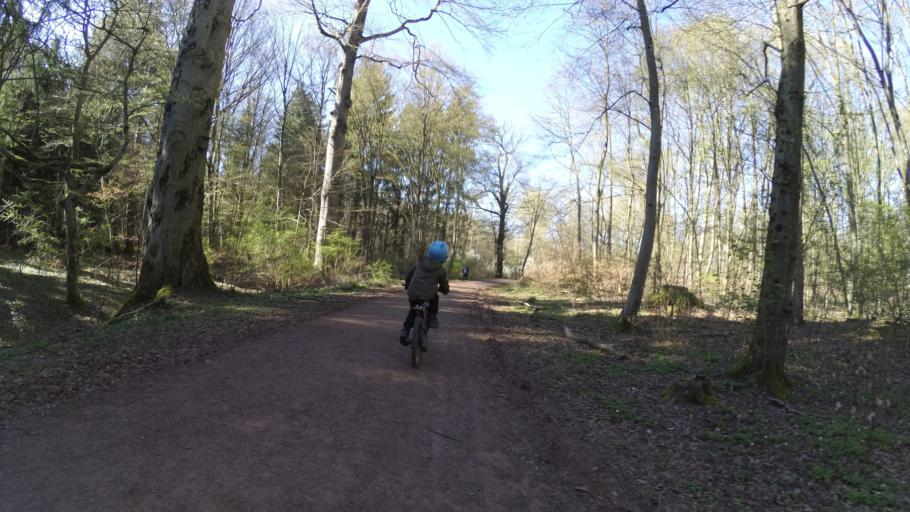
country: DE
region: Saarland
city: Volklingen
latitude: 49.2640
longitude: 6.8750
